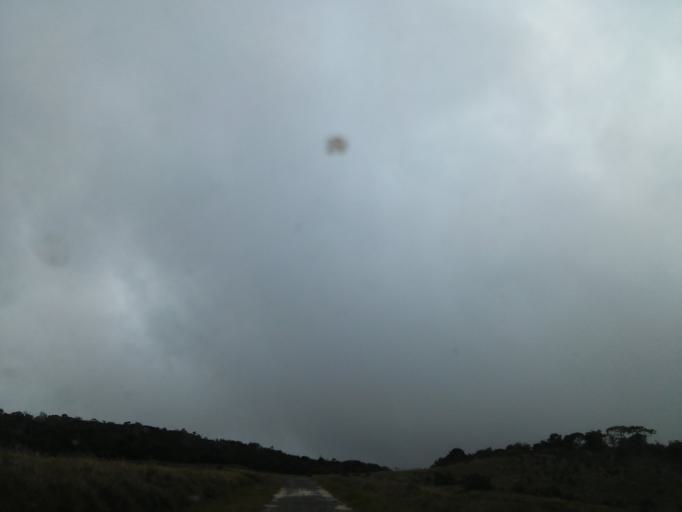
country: LK
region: Uva
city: Haputale
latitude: 6.7949
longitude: 80.8191
